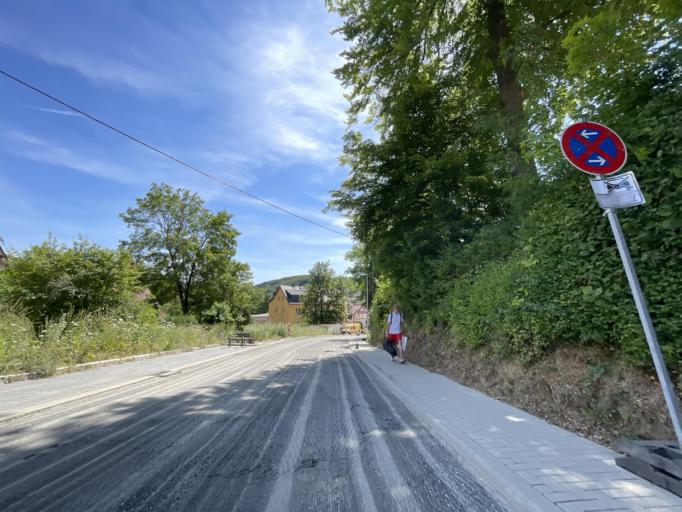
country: GB
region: England
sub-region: East Sussex
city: Eastbourne
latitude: 50.5910
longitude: 0.4533
